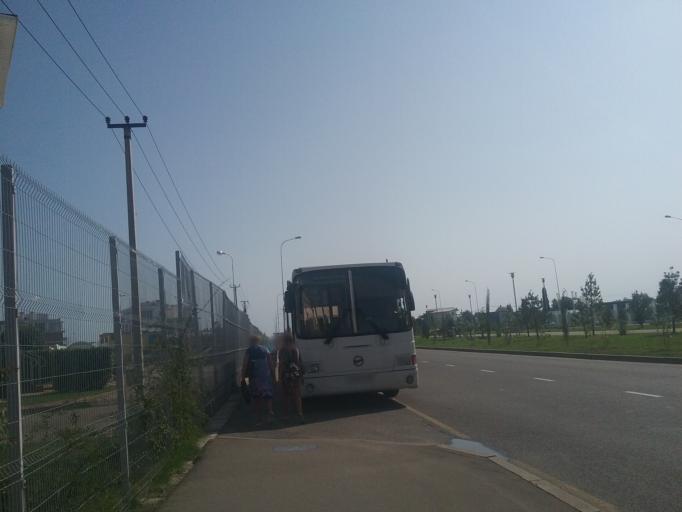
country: RU
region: Krasnodarskiy
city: Vysokoye
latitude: 43.3893
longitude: 39.9911
